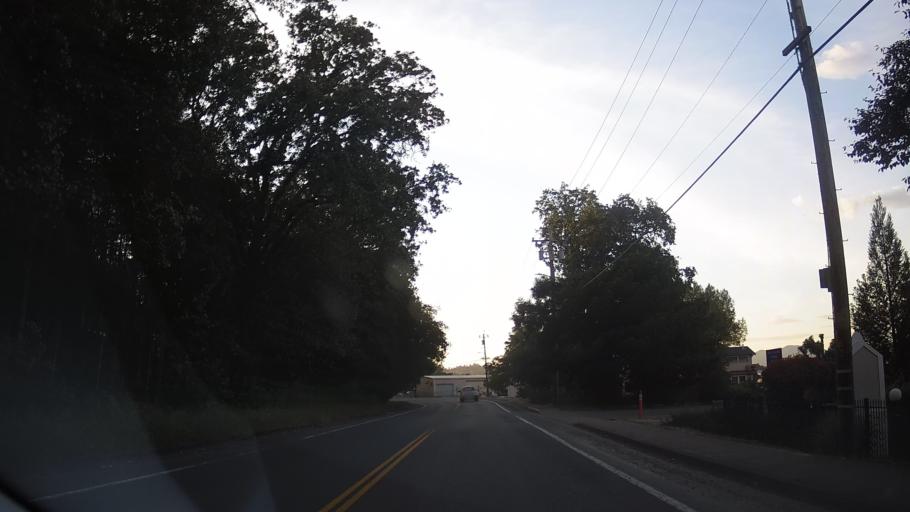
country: US
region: California
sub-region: Mendocino County
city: Willits
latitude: 39.3955
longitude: -123.3445
